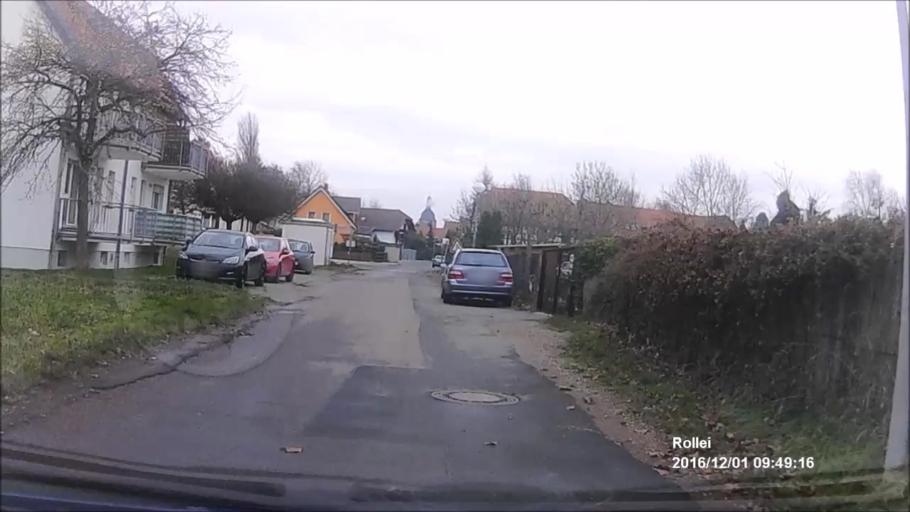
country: DE
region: Thuringia
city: Elxleben
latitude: 51.0378
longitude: 10.9712
